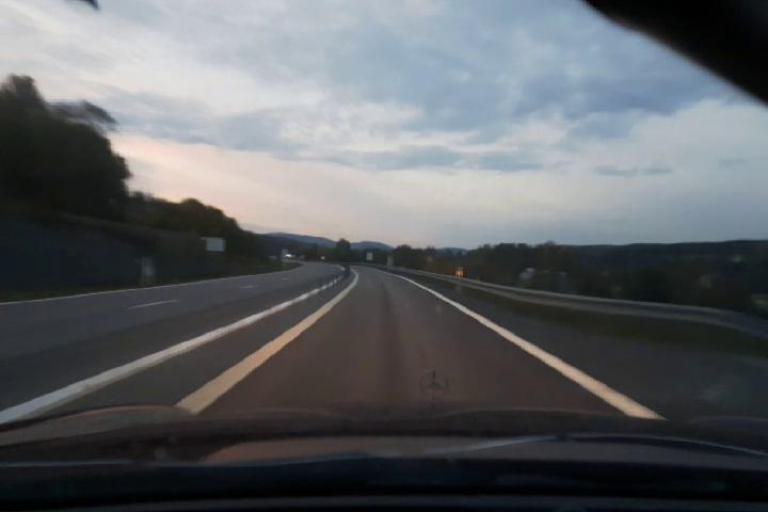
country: SE
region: Vaesternorrland
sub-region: Kramfors Kommun
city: Nordingra
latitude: 62.9752
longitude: 18.1605
